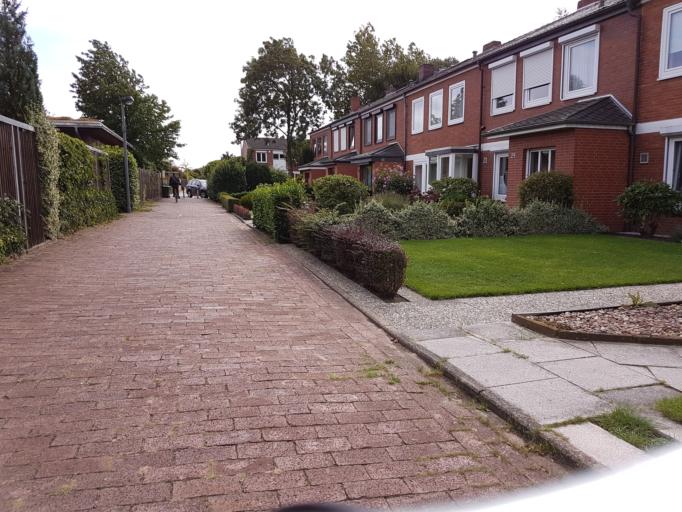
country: DE
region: Lower Saxony
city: Stuhr
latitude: 53.0558
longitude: 8.7613
